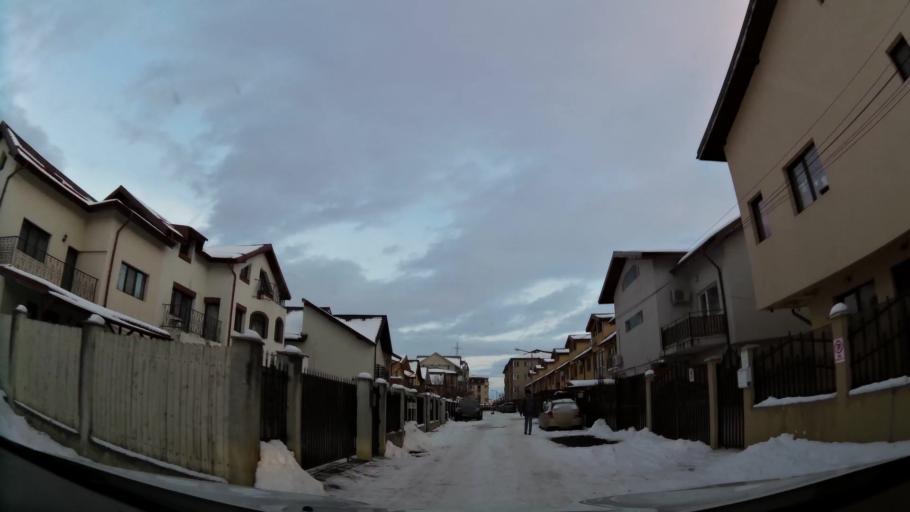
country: RO
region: Ilfov
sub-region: Comuna Popesti-Leordeni
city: Popesti-Leordeni
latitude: 44.3700
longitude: 26.1504
